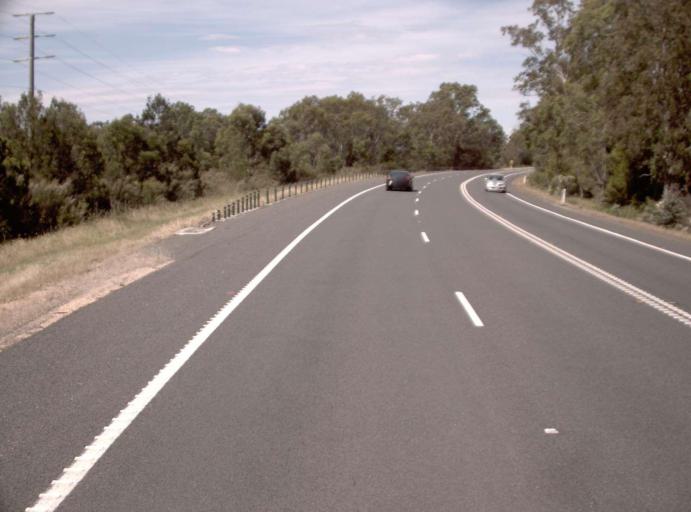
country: AU
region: Victoria
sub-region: Wellington
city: Sale
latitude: -37.9443
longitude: 147.1265
